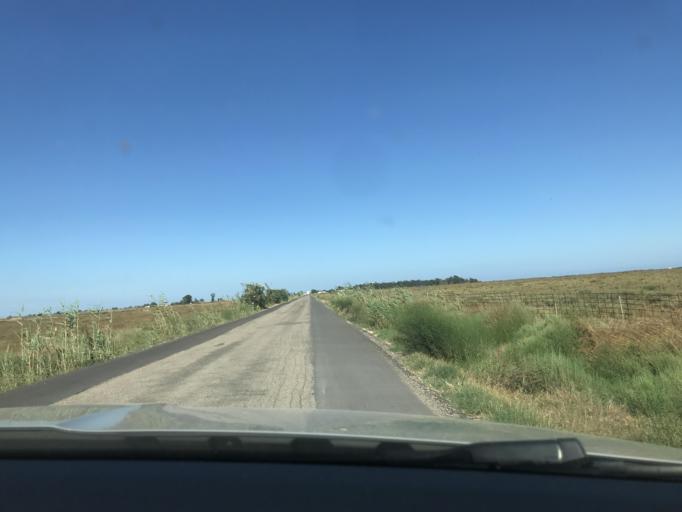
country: ES
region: Catalonia
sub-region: Provincia de Tarragona
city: Deltebre
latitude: 40.6508
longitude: 0.7625
